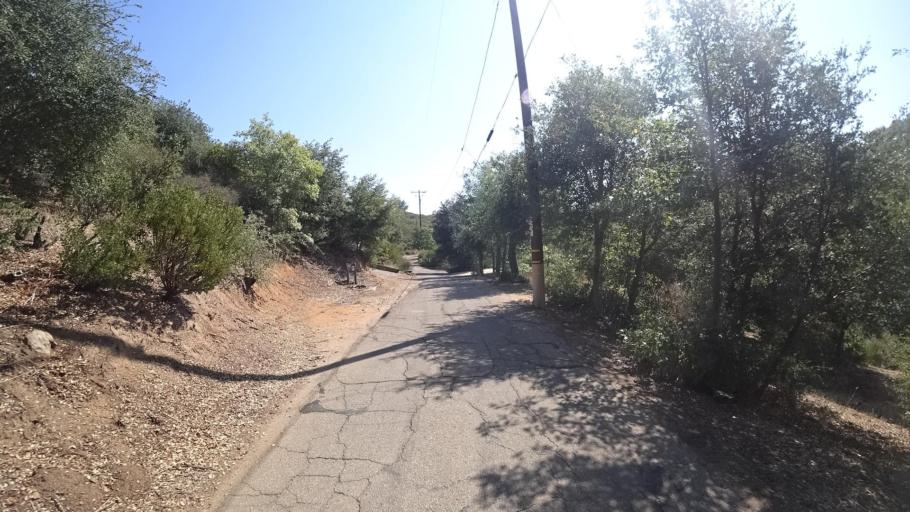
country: US
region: California
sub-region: San Diego County
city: Julian
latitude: 33.0257
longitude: -116.5683
